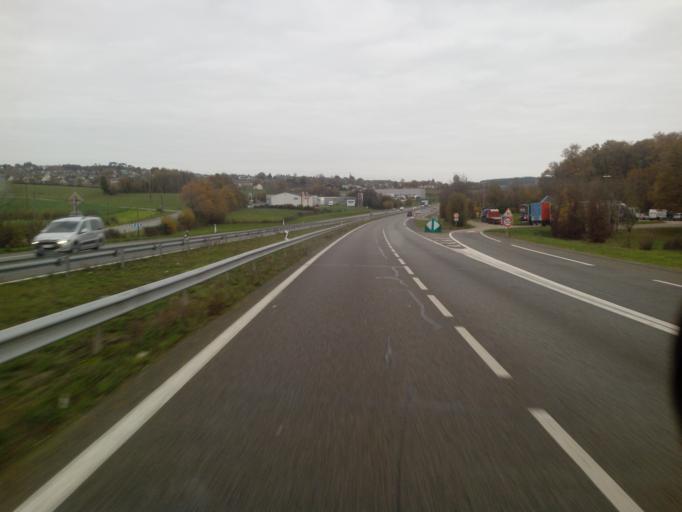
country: FR
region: Brittany
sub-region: Departement d'Ille-et-Vilaine
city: Pance
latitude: 47.8983
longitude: -1.6864
